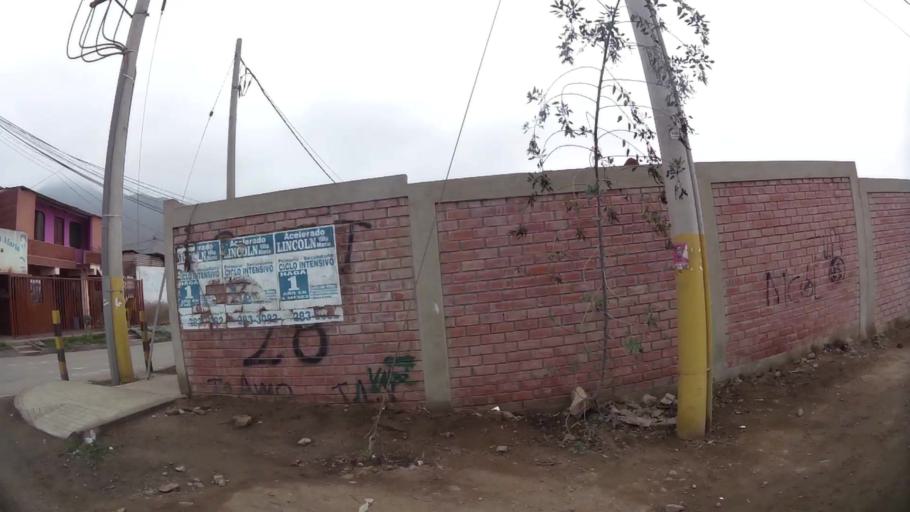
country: PE
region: Lima
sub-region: Lima
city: Cieneguilla
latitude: -12.2087
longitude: -76.9081
